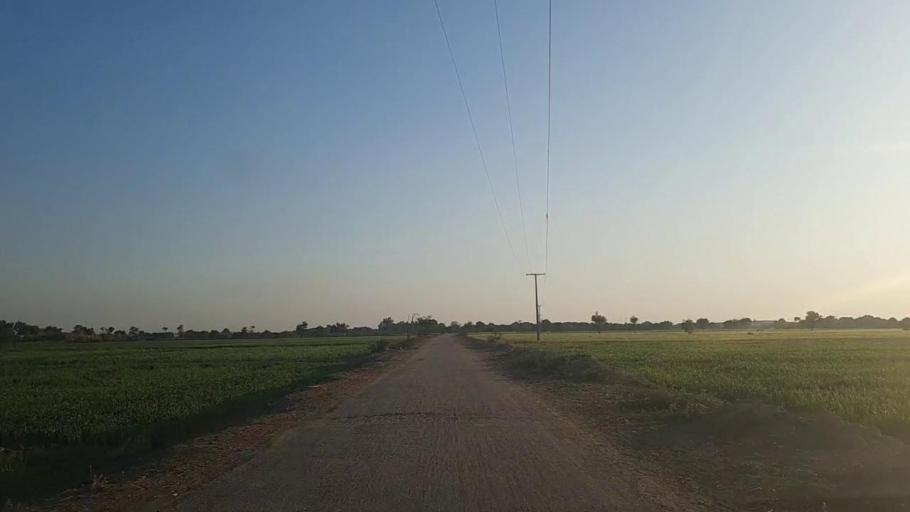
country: PK
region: Sindh
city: Jam Sahib
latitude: 26.3276
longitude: 68.6973
